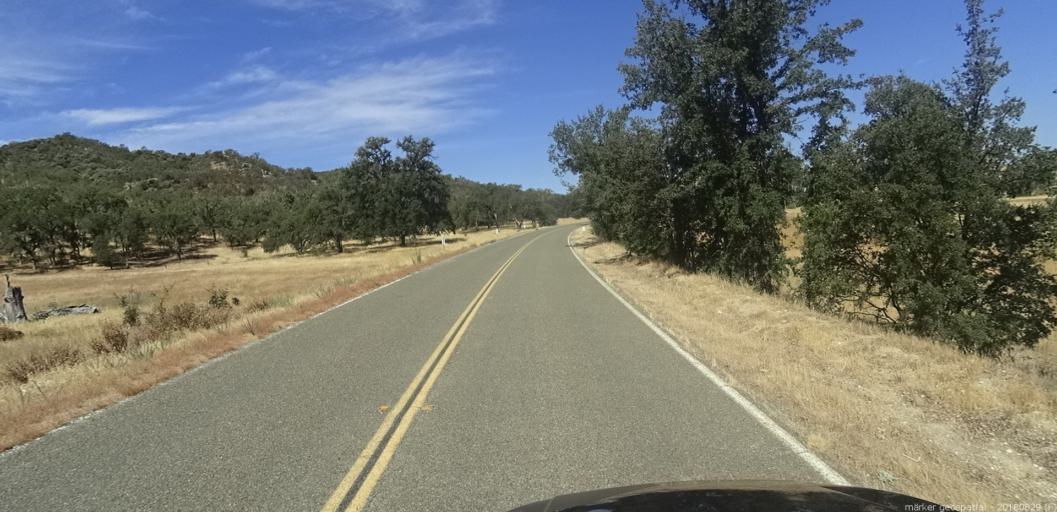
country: US
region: California
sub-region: San Luis Obispo County
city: Lake Nacimiento
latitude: 35.8047
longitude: -120.9915
